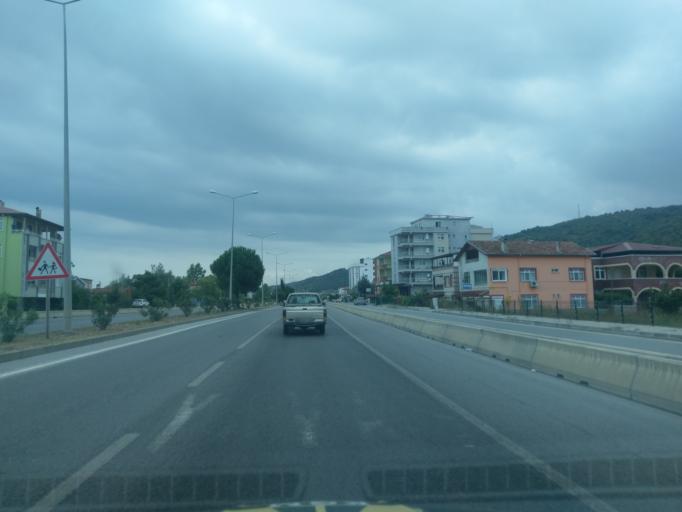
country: TR
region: Samsun
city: Taflan
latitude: 41.3949
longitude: 36.1987
